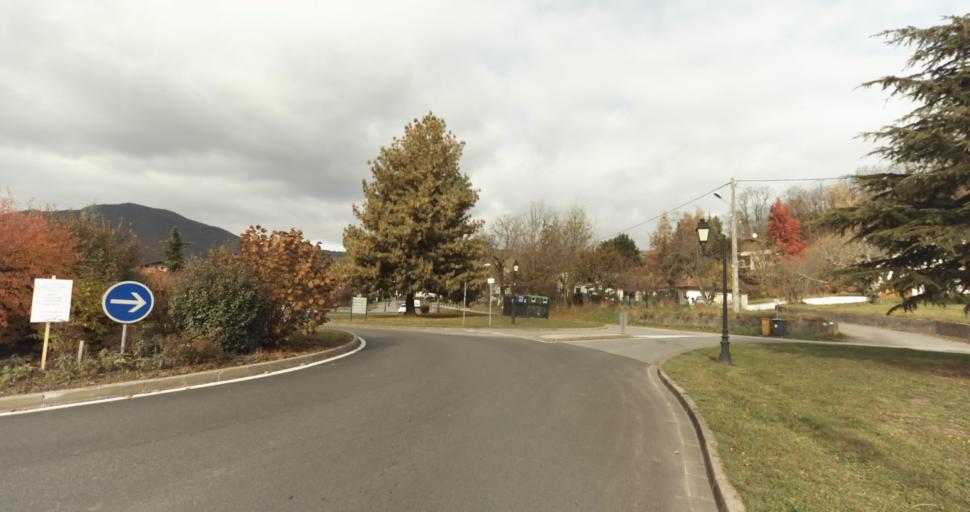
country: FR
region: Rhone-Alpes
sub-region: Departement de la Haute-Savoie
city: Epagny
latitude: 45.9400
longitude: 6.0907
